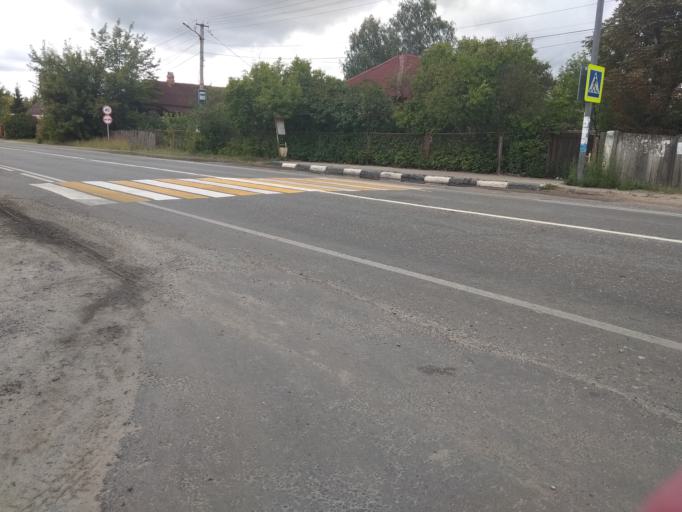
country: RU
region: Moskovskaya
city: Kerva
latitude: 55.5618
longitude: 39.6858
